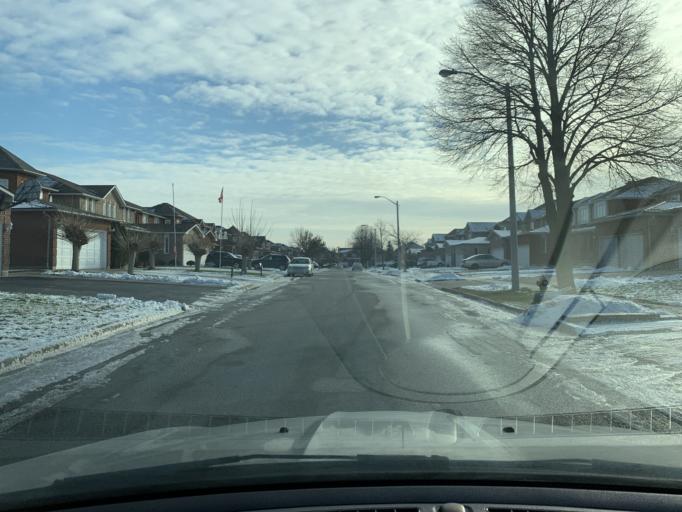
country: CA
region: Ontario
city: Etobicoke
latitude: 43.7227
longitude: -79.6178
